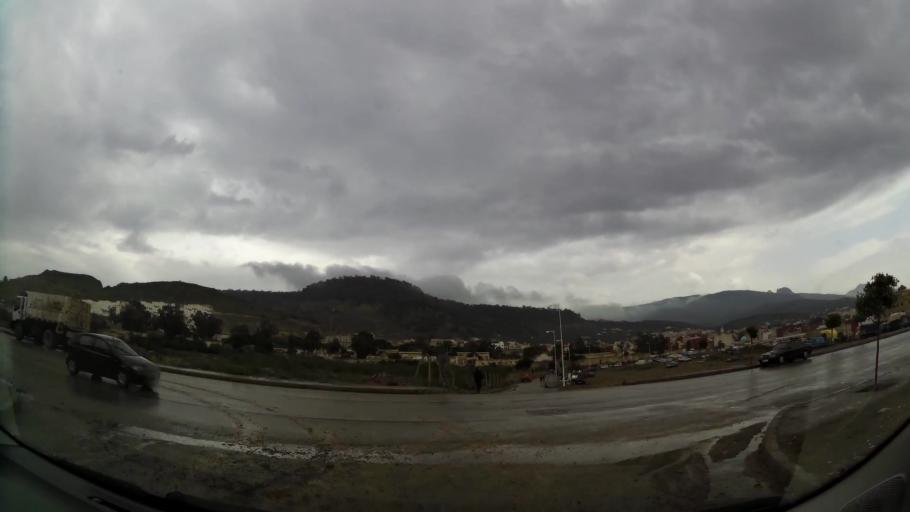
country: MA
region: Oriental
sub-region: Nador
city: Nador
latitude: 35.1480
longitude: -3.0044
